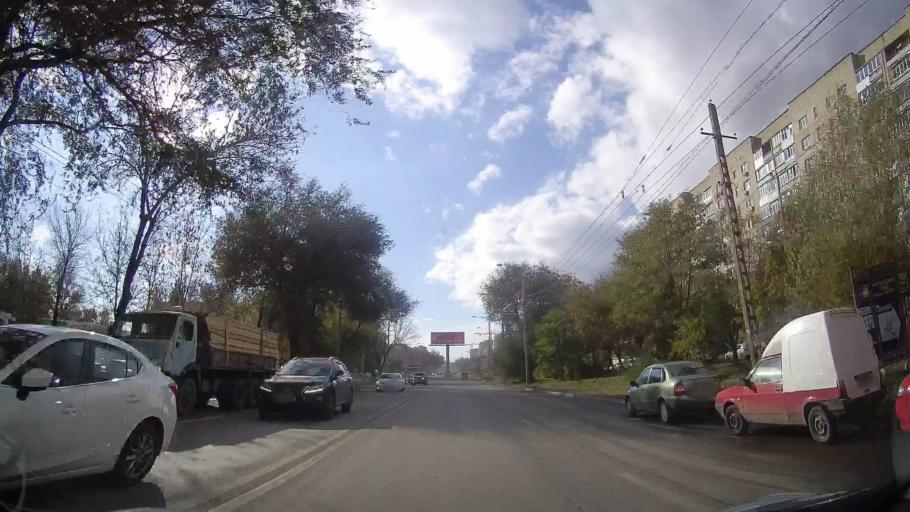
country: RU
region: Rostov
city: Severnyy
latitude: 47.2617
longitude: 39.6552
